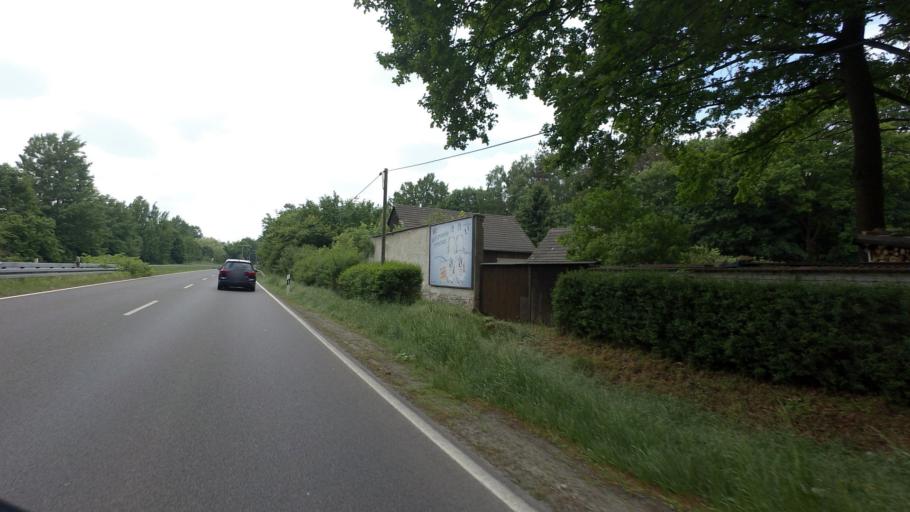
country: DE
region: Brandenburg
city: Cottbus
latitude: 51.7987
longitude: 14.3814
